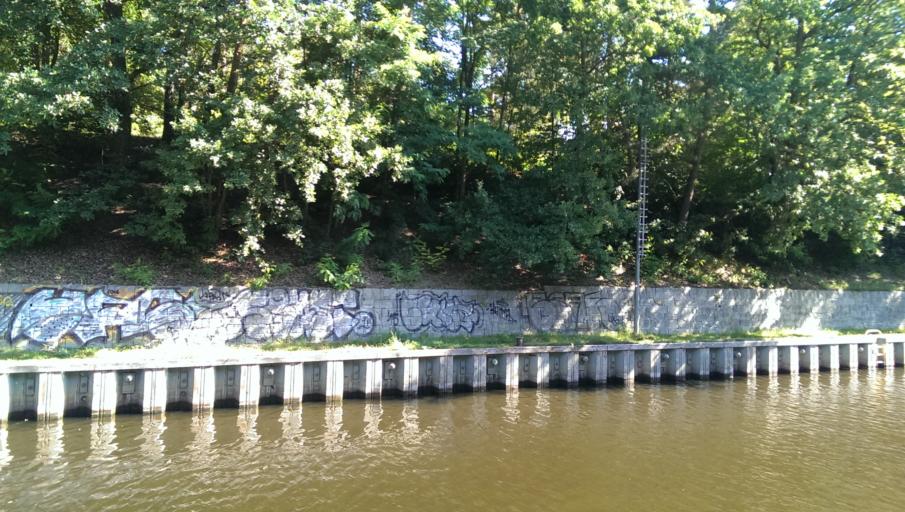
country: DE
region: Berlin
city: Wannsee
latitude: 52.3989
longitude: 13.1454
